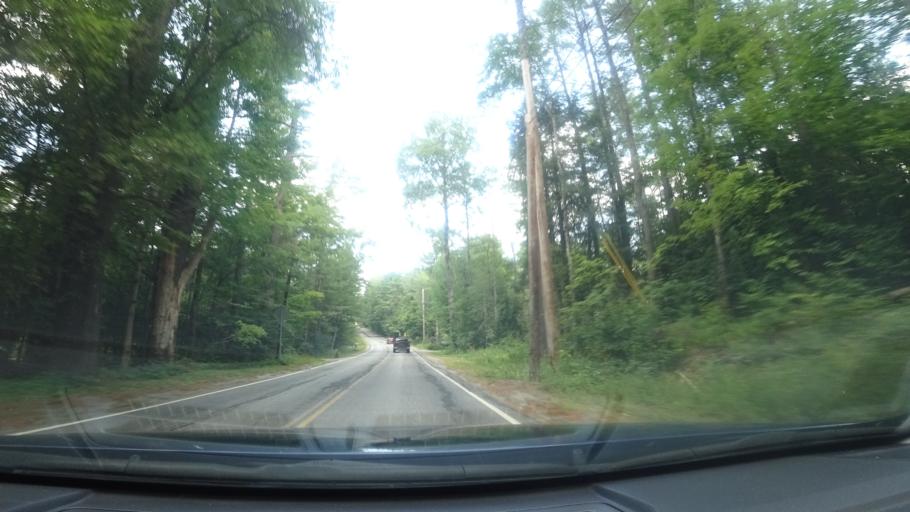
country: US
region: New York
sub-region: Warren County
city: Warrensburg
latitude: 43.6582
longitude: -73.8333
